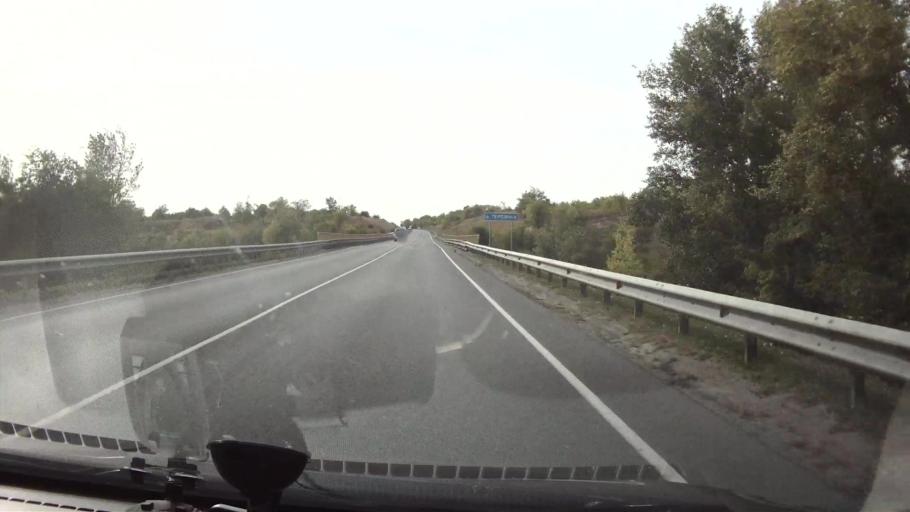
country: RU
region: Saratov
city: Tersa
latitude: 52.0844
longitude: 47.5928
